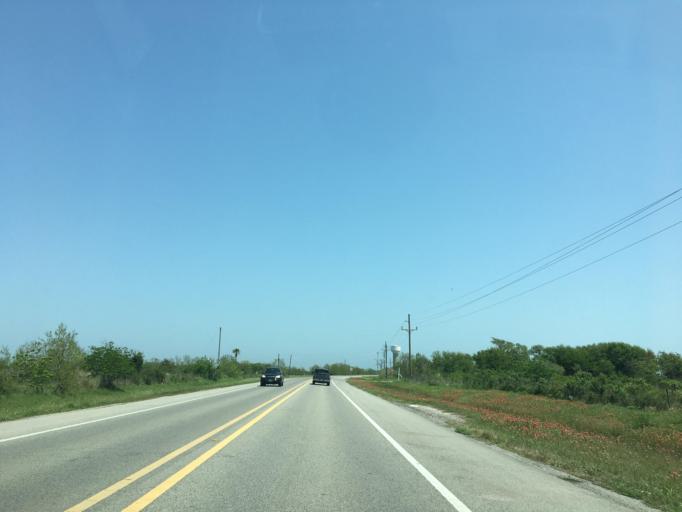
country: US
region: Texas
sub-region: Galveston County
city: Bolivar Peninsula
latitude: 29.4160
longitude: -94.7097
